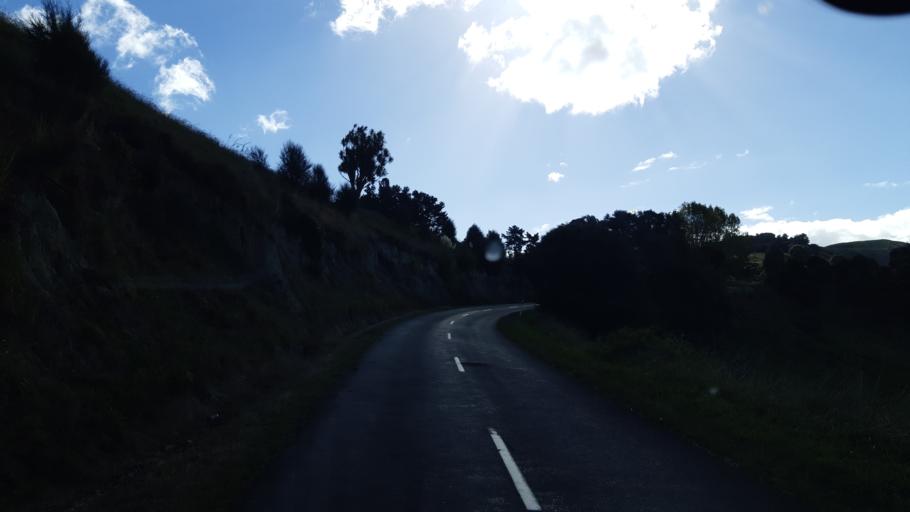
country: NZ
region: Manawatu-Wanganui
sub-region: Rangitikei District
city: Bulls
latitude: -39.9074
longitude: 175.3575
